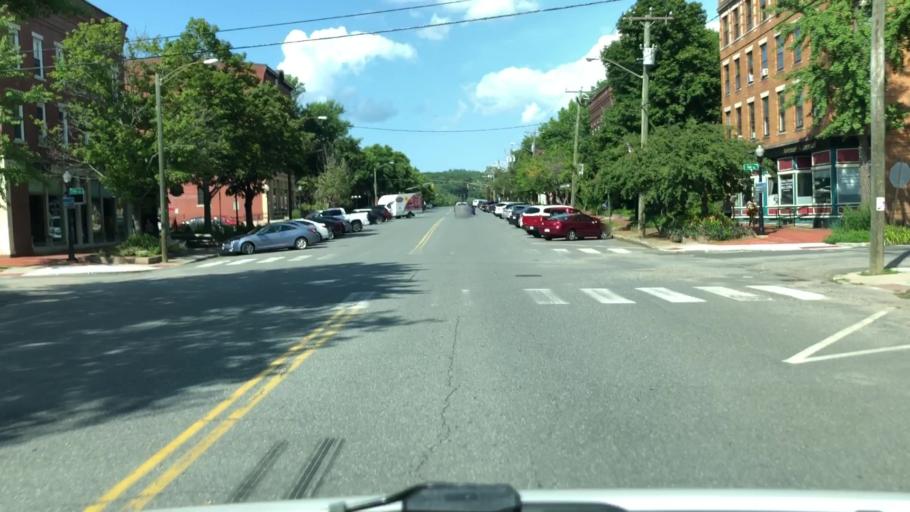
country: US
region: Massachusetts
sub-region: Franklin County
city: Turners Falls
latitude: 42.6067
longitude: -72.5583
